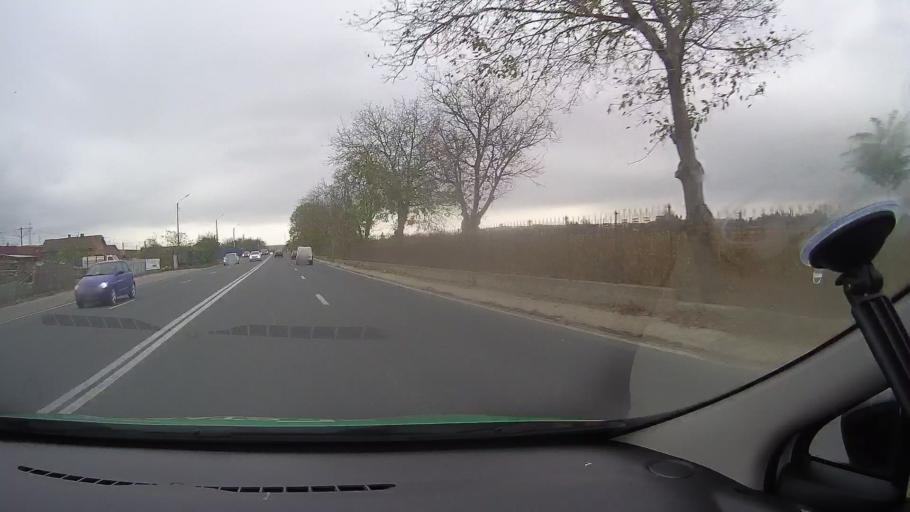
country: RO
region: Constanta
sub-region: Oras Murfatlar
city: Murfatlar
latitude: 44.1714
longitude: 28.4244
